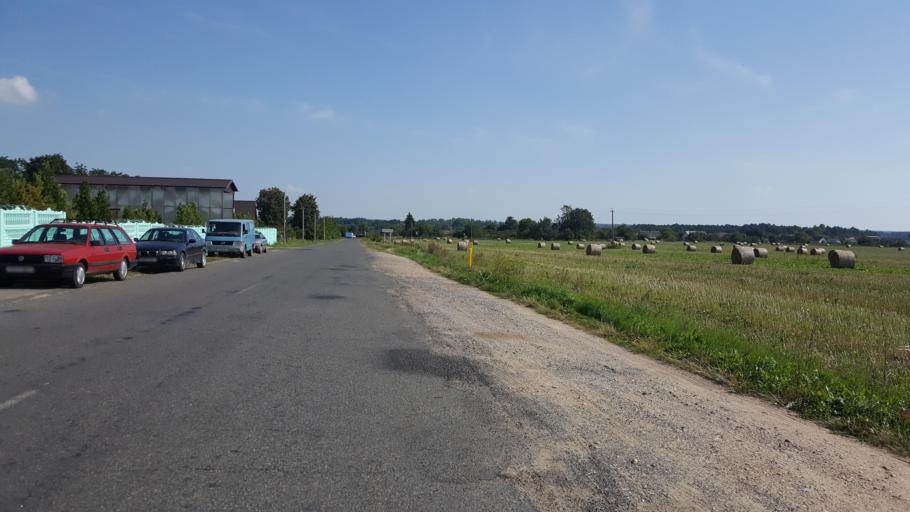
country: BY
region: Brest
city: Kamyanyets
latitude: 52.4095
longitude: 23.7928
